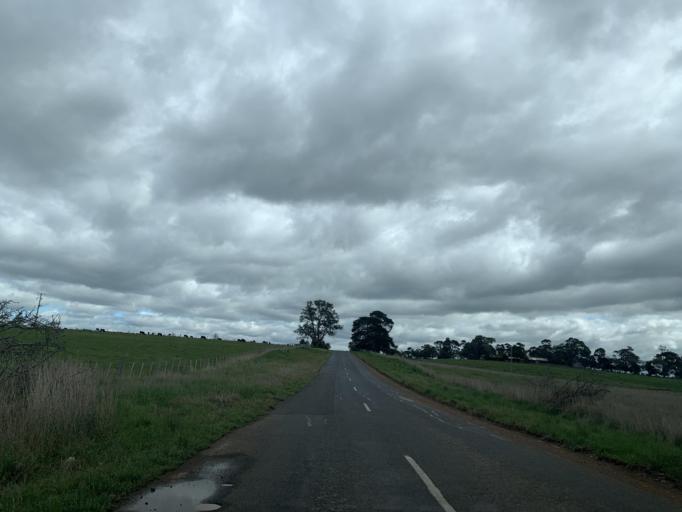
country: AU
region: Victoria
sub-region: Whittlesea
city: Whittlesea
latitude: -37.1859
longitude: 145.0309
